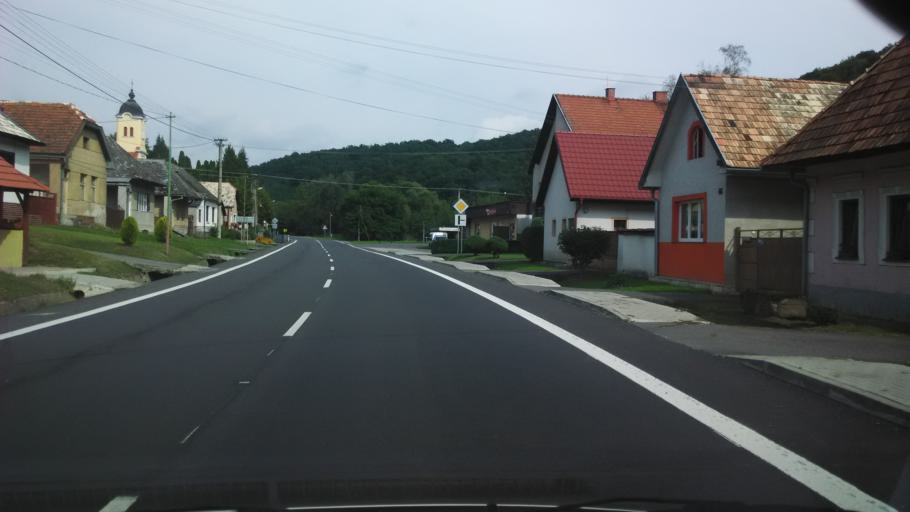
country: SK
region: Banskobystricky
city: Krupina
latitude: 48.2634
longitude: 18.9899
